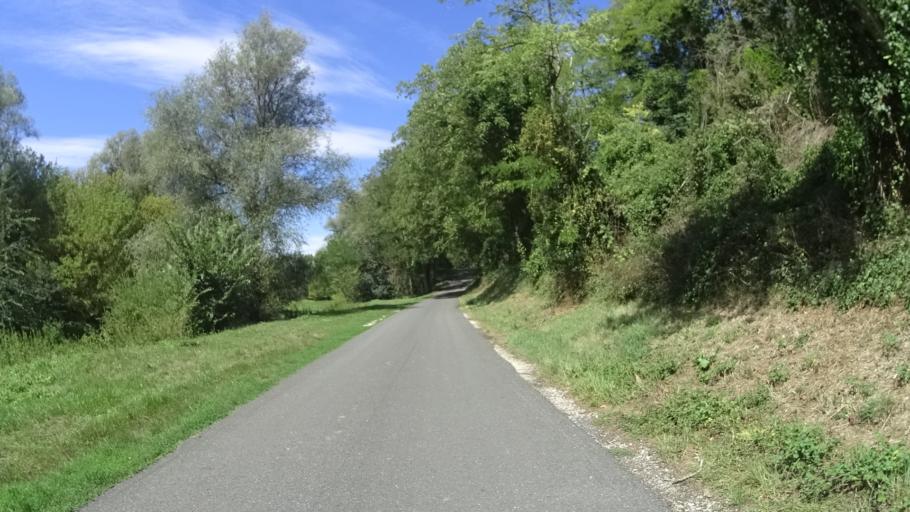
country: FR
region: Centre
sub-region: Departement du Loiret
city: Bonny-sur-Loire
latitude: 47.5765
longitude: 2.8140
